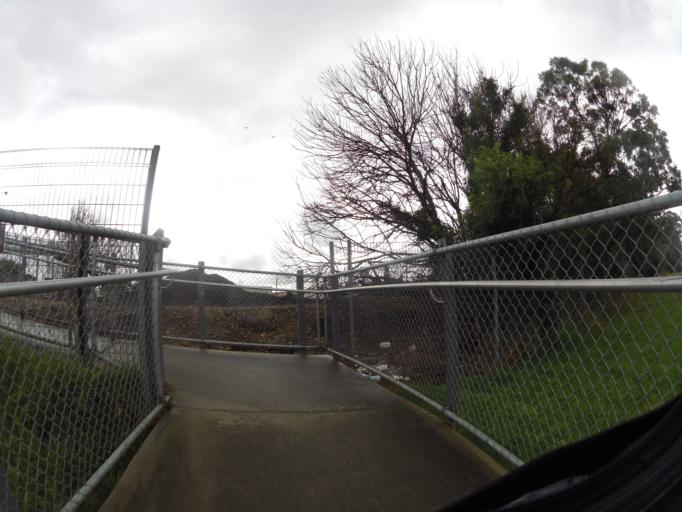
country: AU
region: Victoria
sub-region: East Gippsland
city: Bairnsdale
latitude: -37.8297
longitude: 147.6255
